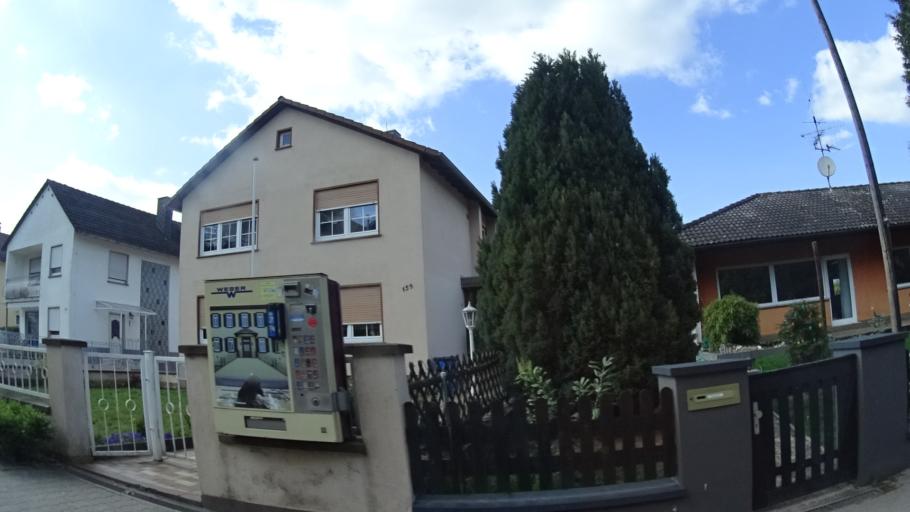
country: DE
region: Rheinland-Pfalz
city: Dexheim
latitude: 49.8635
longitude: 8.3066
